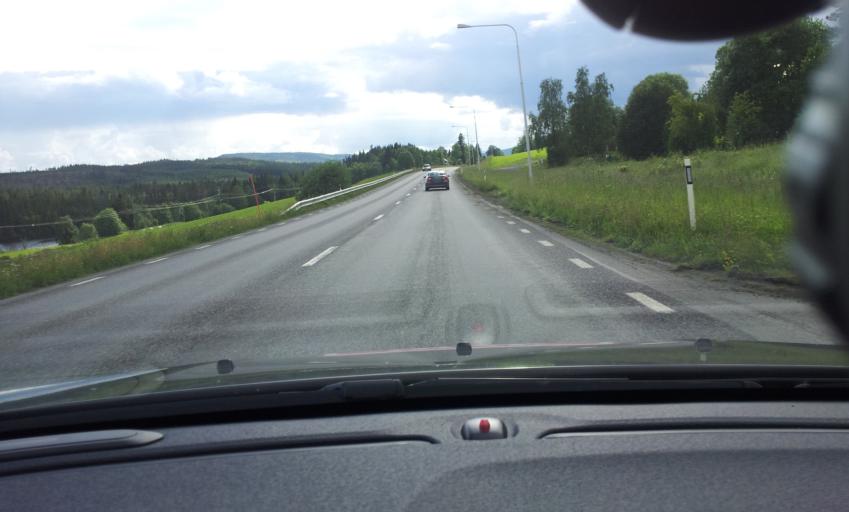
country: SE
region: Jaemtland
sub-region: Are Kommun
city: Jarpen
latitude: 63.3318
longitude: 13.4097
